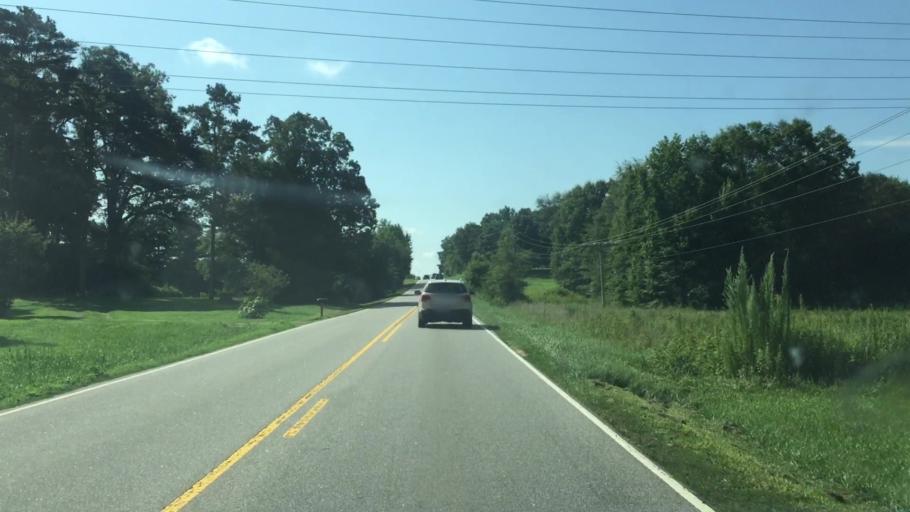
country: US
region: North Carolina
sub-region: Union County
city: Unionville
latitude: 35.1261
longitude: -80.4302
